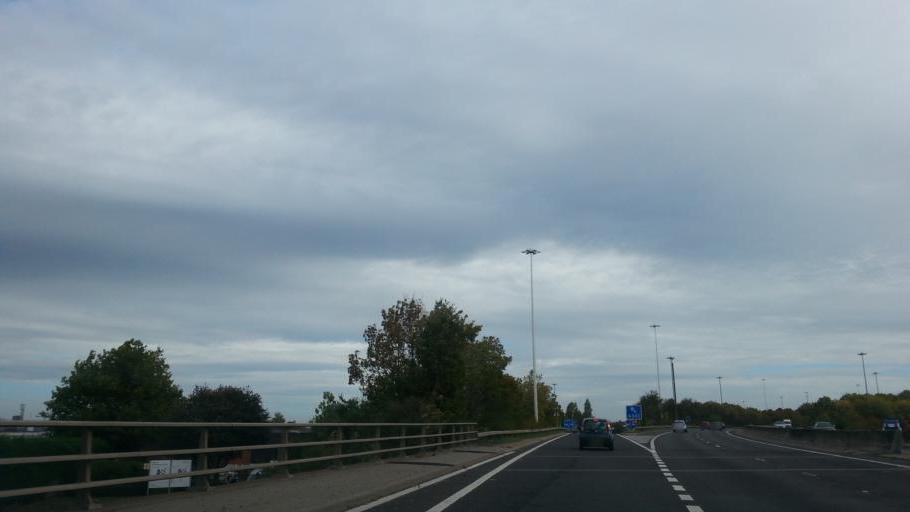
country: GB
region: England
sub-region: City and Borough of Leeds
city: Leeds
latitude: 53.7797
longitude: -1.5729
